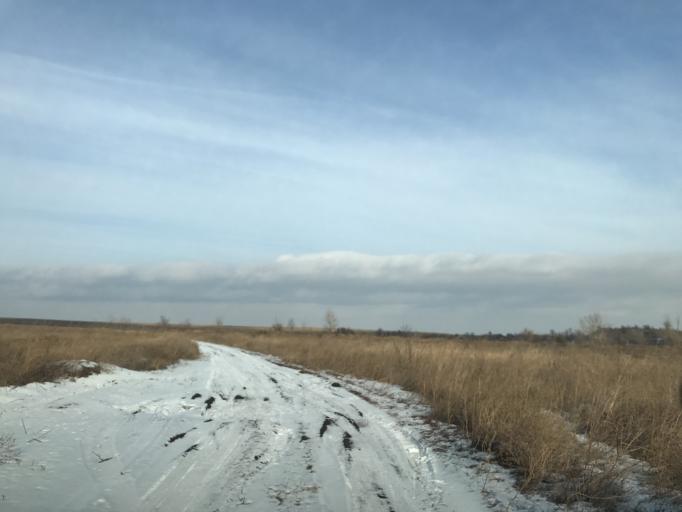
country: RU
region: Rostov
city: Staraya Stanitsa
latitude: 48.2435
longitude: 40.3995
